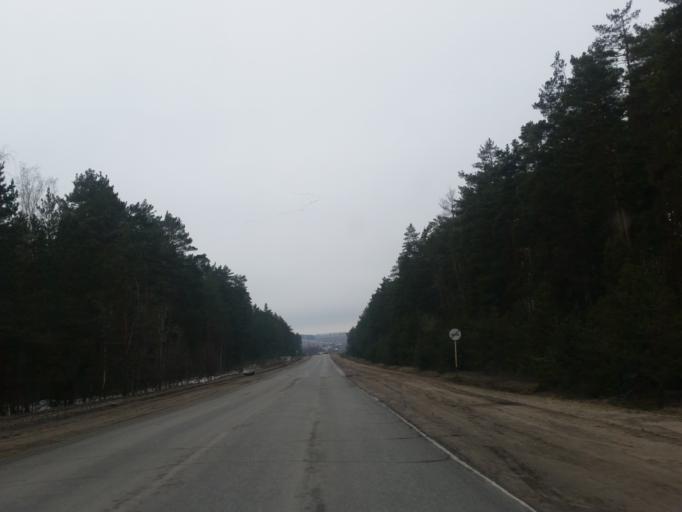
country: RU
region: Ulyanovsk
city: Mullovka
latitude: 54.2235
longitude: 49.4182
